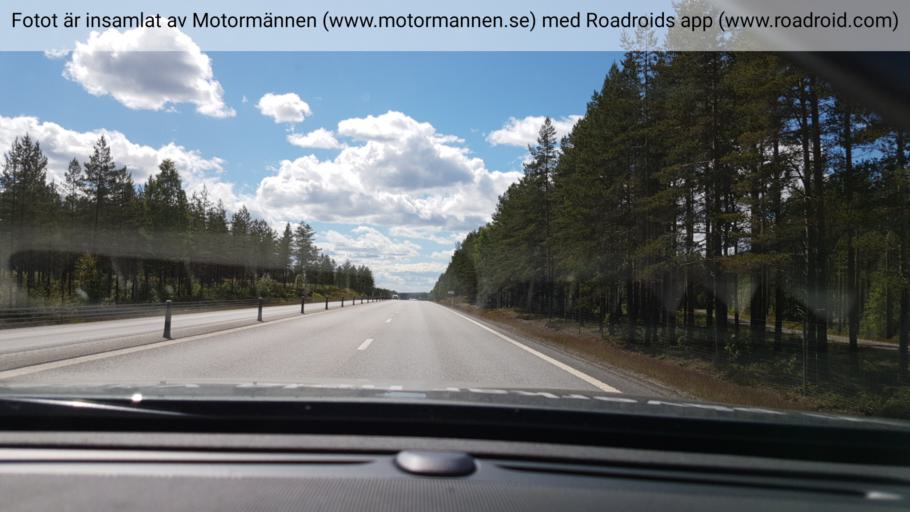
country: SE
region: Vaesterbotten
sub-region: Umea Kommun
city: Taftea
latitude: 63.8810
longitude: 20.4860
